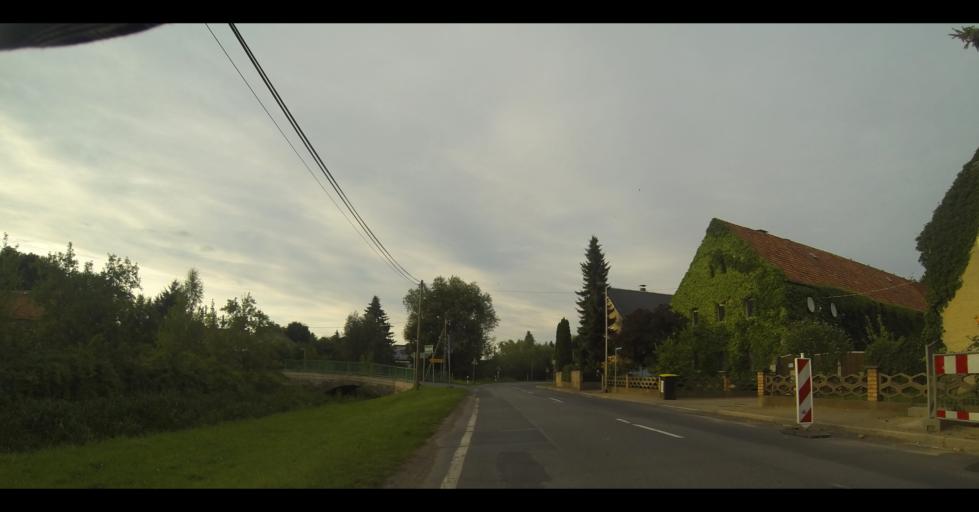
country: DE
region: Saxony
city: Radeburg
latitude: 51.1903
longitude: 13.7253
